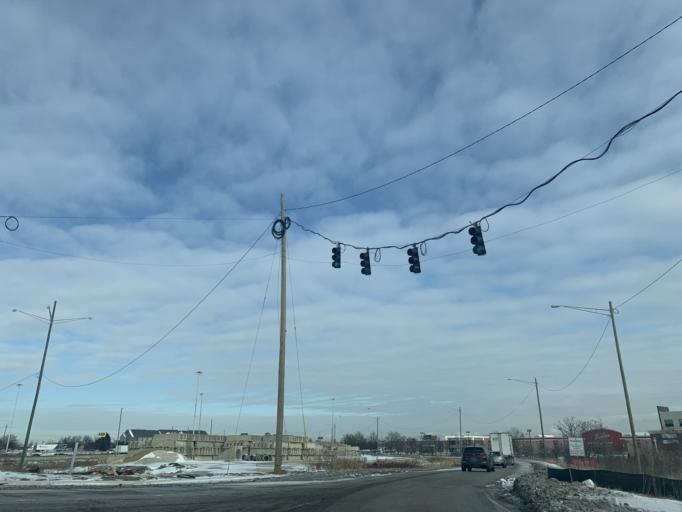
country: US
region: Illinois
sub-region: Will County
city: Romeoville
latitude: 41.6539
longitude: -88.1247
